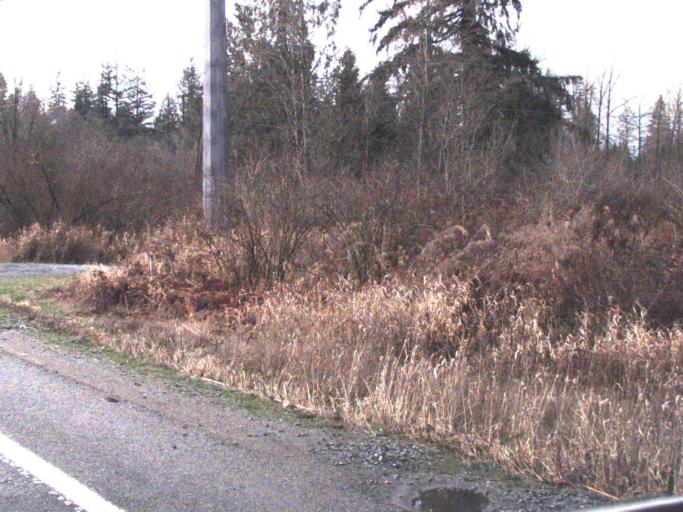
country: US
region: Washington
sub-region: Snohomish County
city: Lochsloy
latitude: 48.0411
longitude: -122.0441
